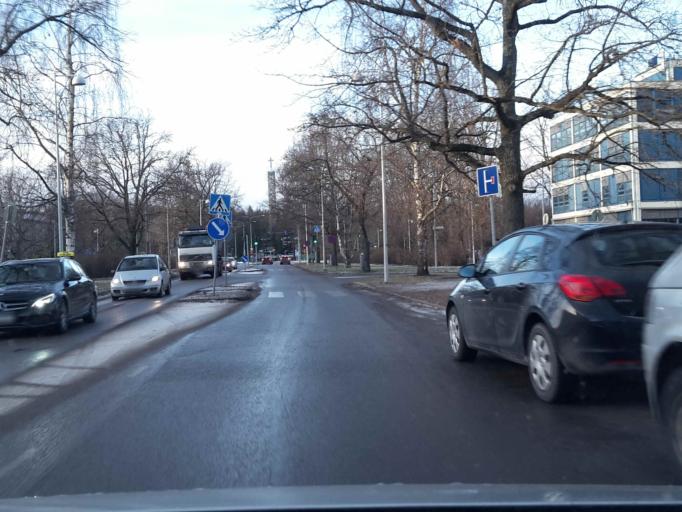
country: FI
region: Uusimaa
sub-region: Helsinki
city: Teekkarikylae
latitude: 60.1579
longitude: 24.8778
